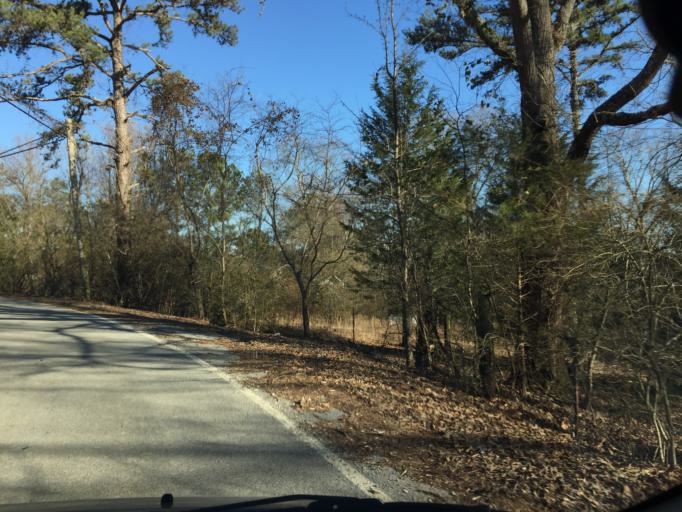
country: US
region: Tennessee
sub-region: Hamilton County
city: Collegedale
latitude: 35.0532
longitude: -85.1114
